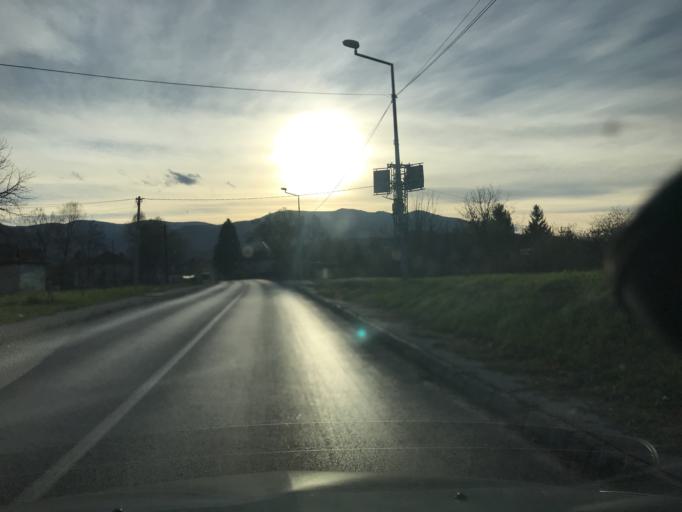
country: BA
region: Federation of Bosnia and Herzegovina
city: Vitez
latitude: 44.1497
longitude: 17.8055
